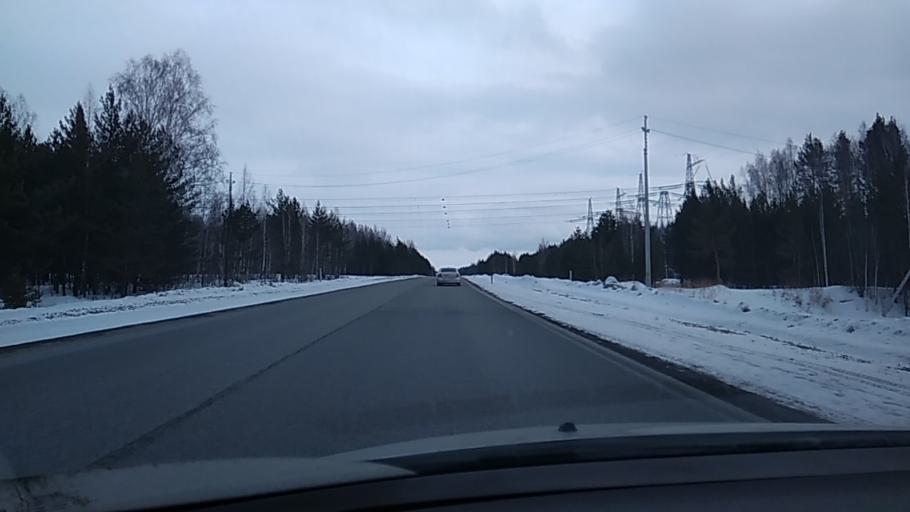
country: RU
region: Sverdlovsk
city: Sovkhoznyy
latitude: 56.5397
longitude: 61.3980
